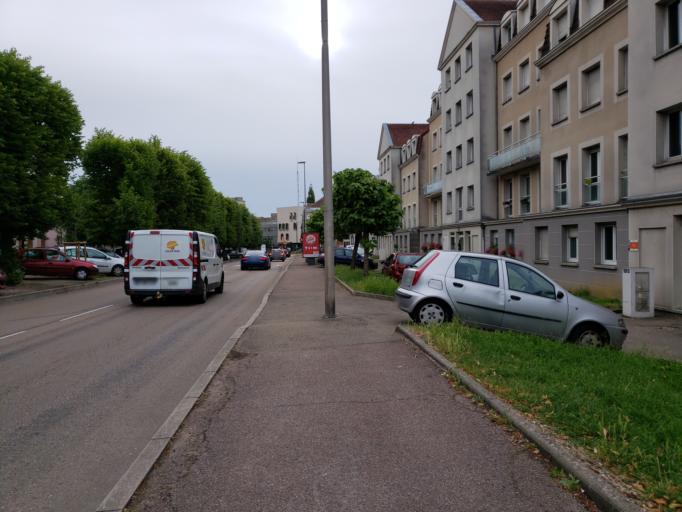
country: FR
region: Bourgogne
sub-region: Departement de l'Yonne
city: Auxerre
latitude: 47.7929
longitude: 3.5761
